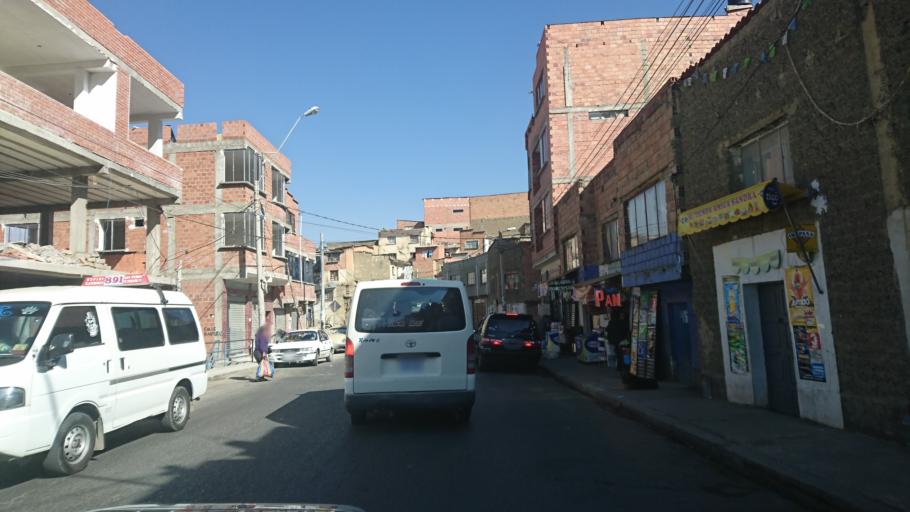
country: BO
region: La Paz
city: La Paz
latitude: -16.5099
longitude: -68.1068
